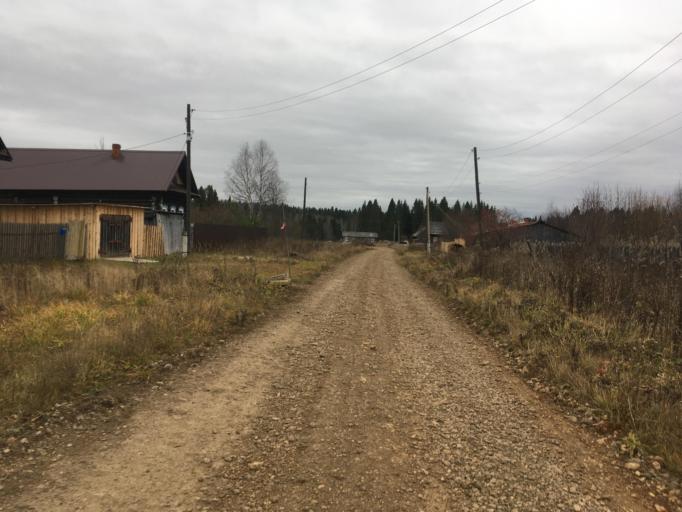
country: RU
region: Perm
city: Komarikhinskiy
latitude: 58.0895
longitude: 57.1099
